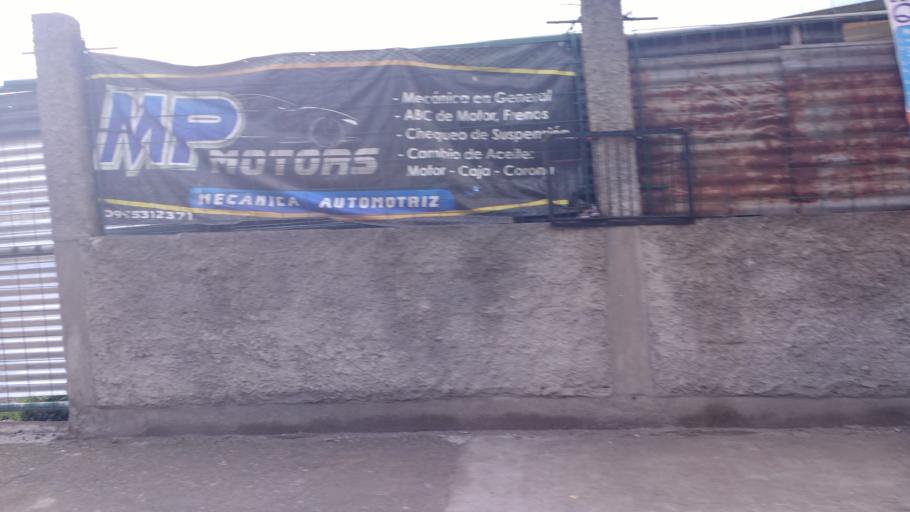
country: EC
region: Azuay
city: Cuenca
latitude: -2.8961
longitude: -79.0526
